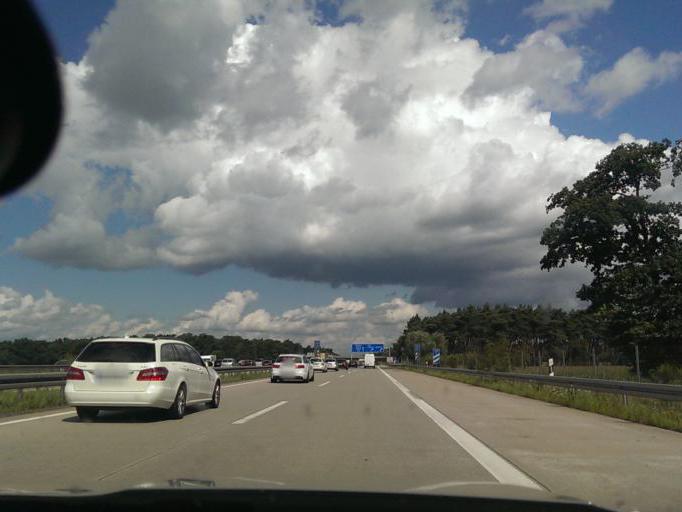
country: DE
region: Lower Saxony
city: Elze
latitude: 52.5511
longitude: 9.7952
